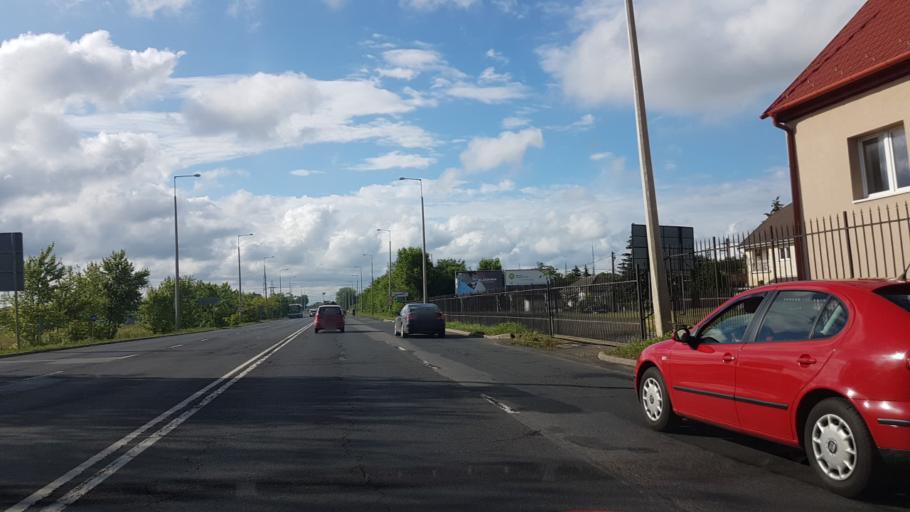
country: HU
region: Hajdu-Bihar
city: Debrecen
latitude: 47.5623
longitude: 21.6016
